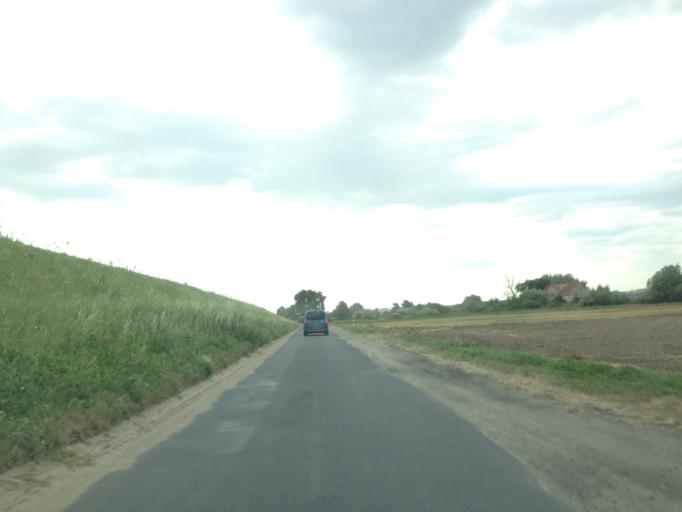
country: PL
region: Kujawsko-Pomorskie
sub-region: Powiat chelminski
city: Chelmno
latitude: 53.3650
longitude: 18.3887
